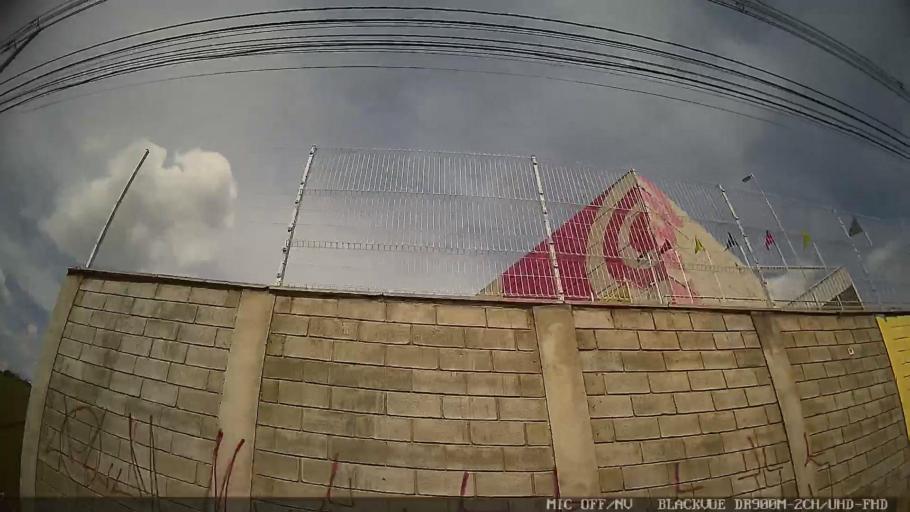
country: BR
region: Sao Paulo
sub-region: Braganca Paulista
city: Braganca Paulista
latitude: -22.9488
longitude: -46.5286
